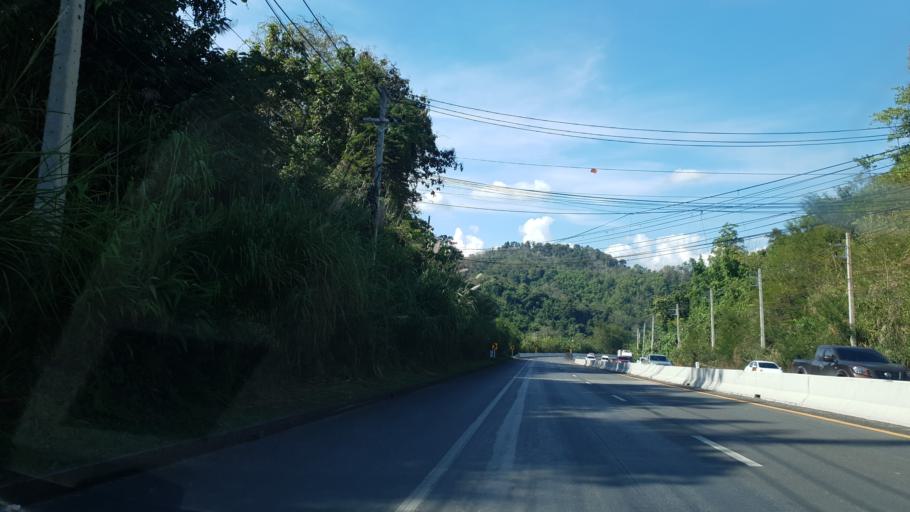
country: TH
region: Phrae
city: Den Chai
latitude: 17.8488
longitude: 100.0471
